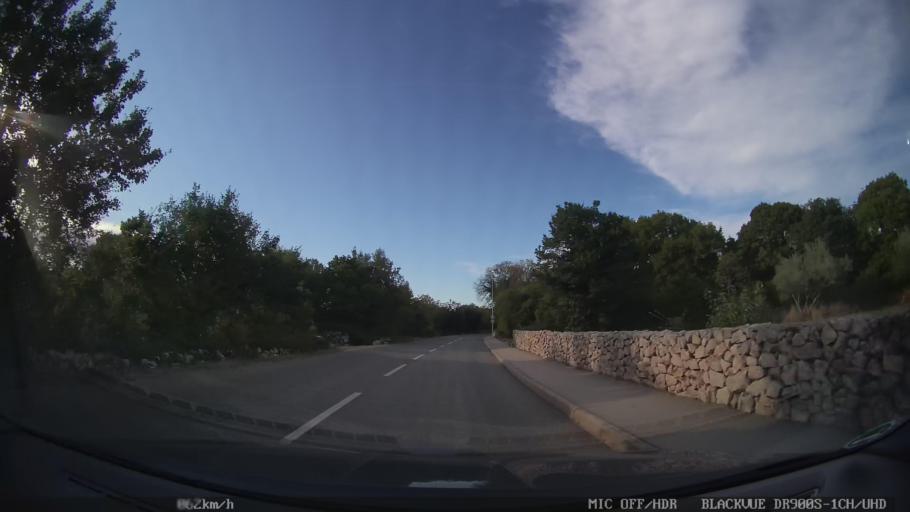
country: HR
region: Primorsko-Goranska
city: Njivice
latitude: 45.1092
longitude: 14.5240
